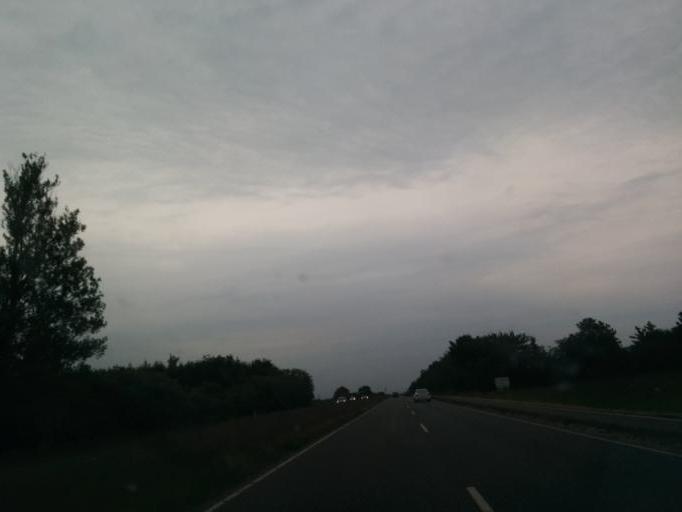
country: DK
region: Central Jutland
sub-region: Arhus Kommune
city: Hjortshoj
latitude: 56.2349
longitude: 10.2971
